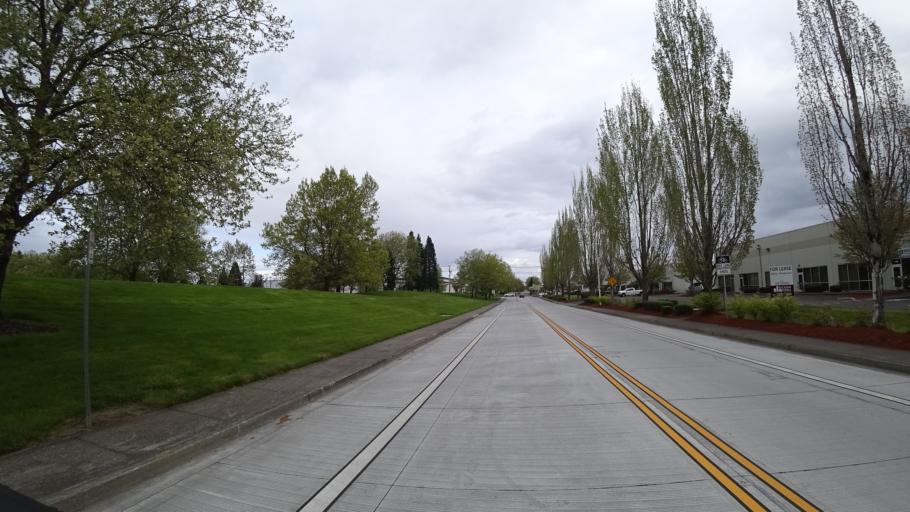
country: US
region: Oregon
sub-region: Washington County
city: Hillsboro
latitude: 45.5401
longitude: -122.9591
